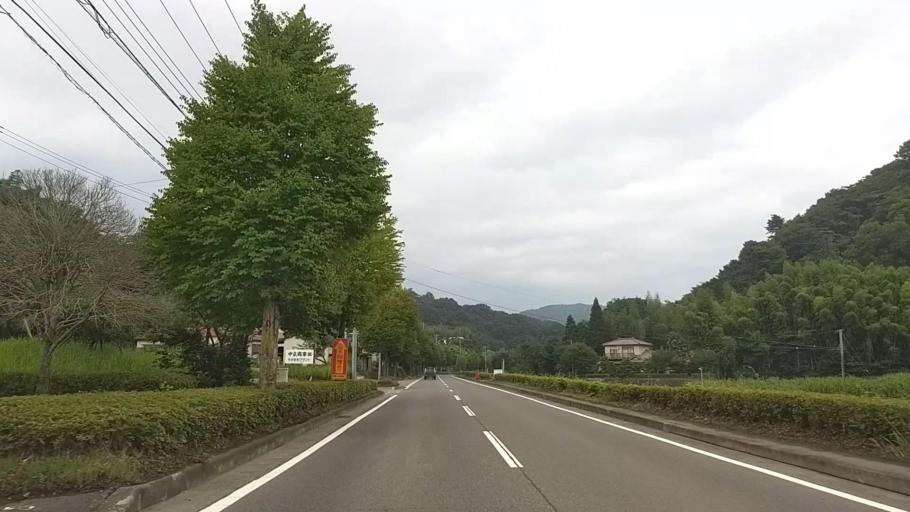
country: JP
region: Kanagawa
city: Hadano
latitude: 35.3330
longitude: 139.2024
